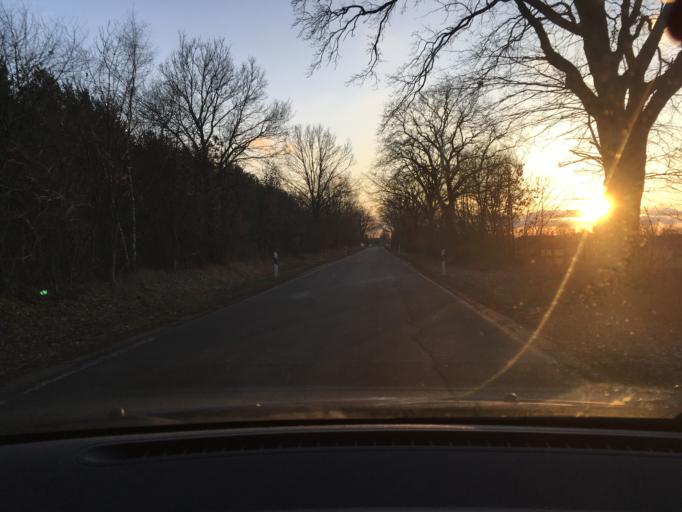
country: DE
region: Schleswig-Holstein
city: Brothen
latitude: 53.4843
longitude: 10.6720
